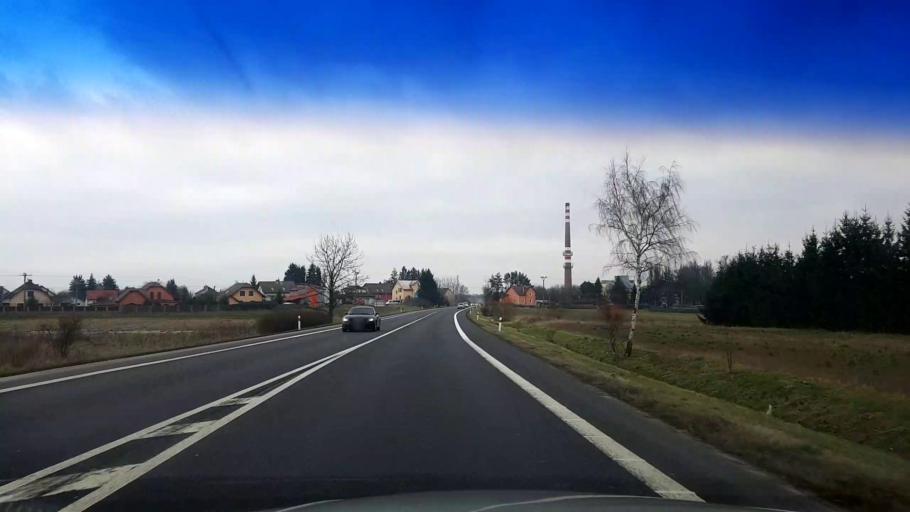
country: CZ
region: Karlovarsky
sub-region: Okres Cheb
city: Frantiskovy Lazne
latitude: 50.1309
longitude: 12.3491
